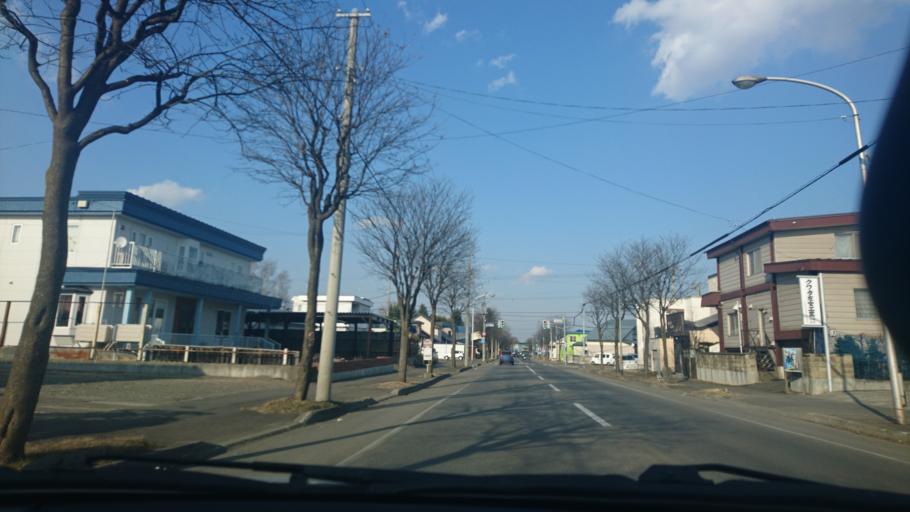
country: JP
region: Hokkaido
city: Obihiro
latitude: 42.9236
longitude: 143.1587
